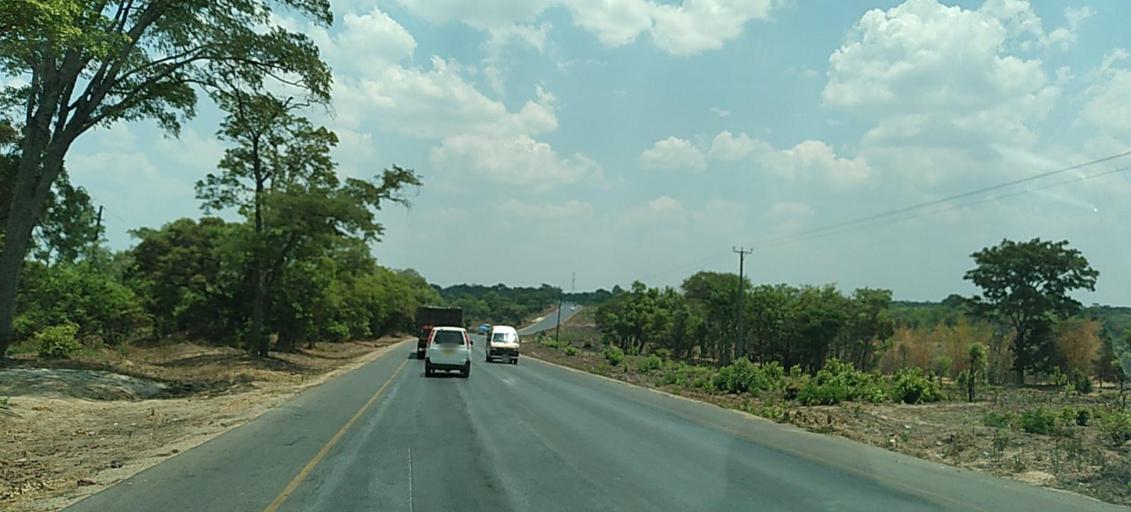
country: ZM
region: Central
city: Kapiri Mposhi
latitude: -14.2097
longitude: 28.5833
